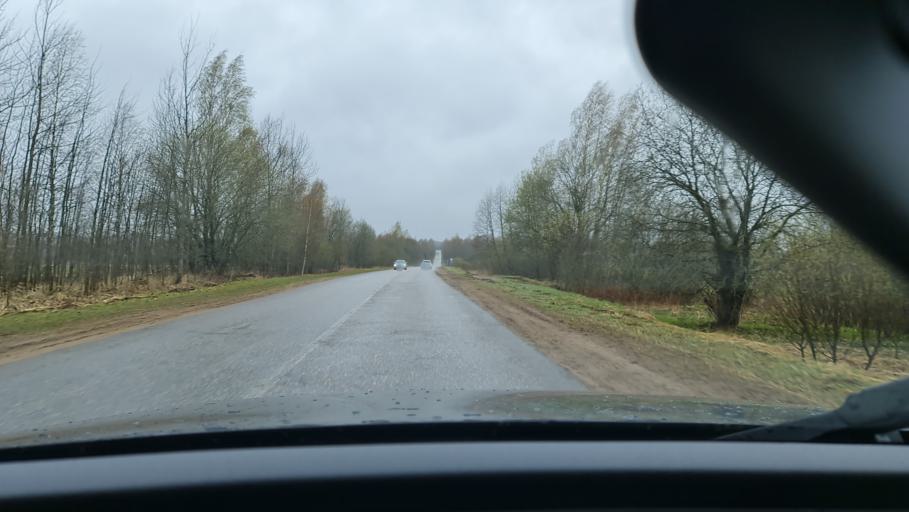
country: RU
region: Novgorod
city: Kresttsy
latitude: 57.9753
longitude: 32.7326
